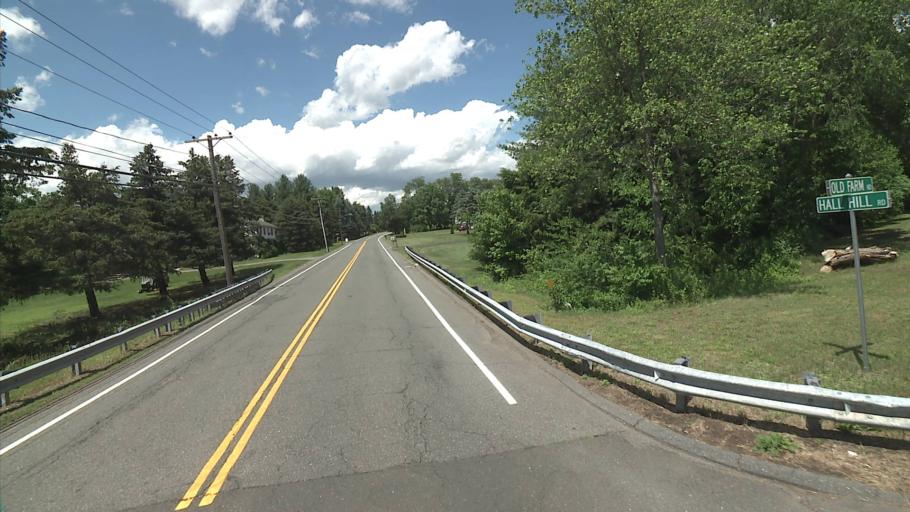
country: US
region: Connecticut
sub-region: Tolland County
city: Somers
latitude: 41.9994
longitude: -72.4882
